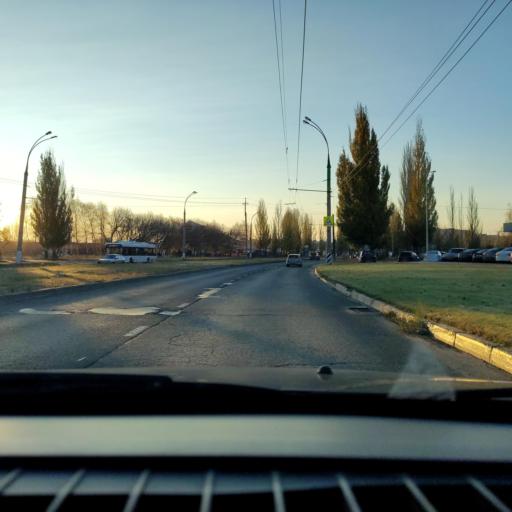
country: RU
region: Samara
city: Tol'yatti
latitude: 53.5441
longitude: 49.2779
